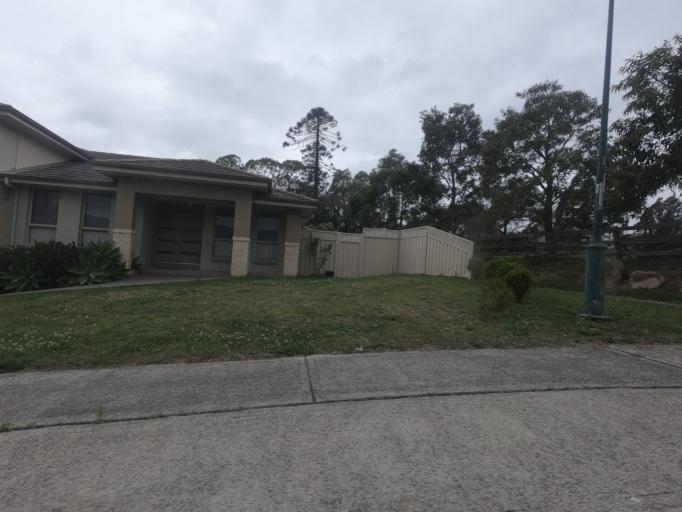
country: AU
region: New South Wales
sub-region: Wollongong
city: Dapto
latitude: -34.4849
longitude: 150.7784
